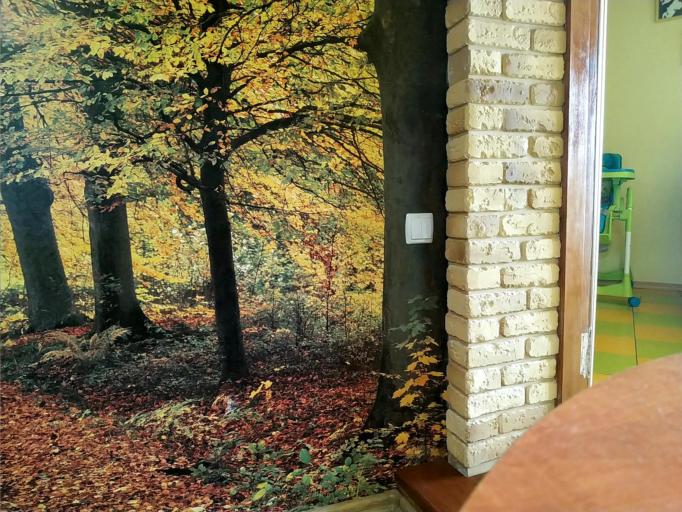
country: RU
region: Smolensk
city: Ozernyy
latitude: 55.4425
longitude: 32.6710
